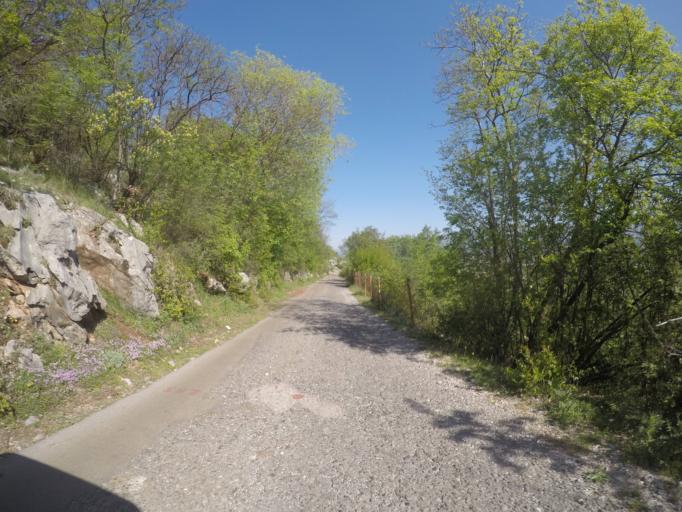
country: ME
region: Danilovgrad
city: Danilovgrad
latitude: 42.5260
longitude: 19.0946
